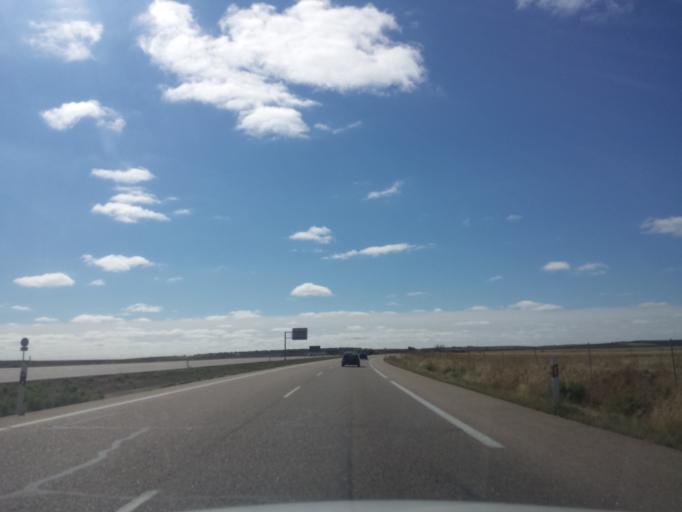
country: ES
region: Castille and Leon
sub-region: Provincia de Zamora
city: Villalpando
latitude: 41.8504
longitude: -5.4041
